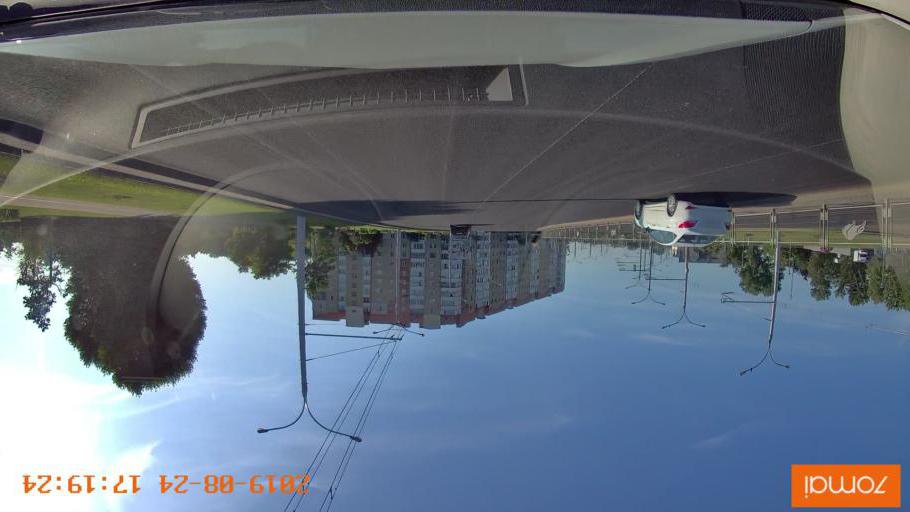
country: BY
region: Minsk
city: Vyaliki Trastsyanets
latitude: 53.8620
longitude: 27.6412
